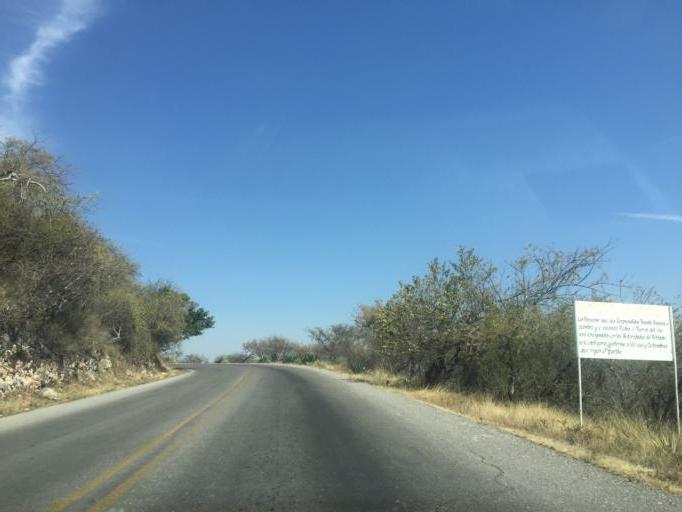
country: MX
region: Morelos
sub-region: Miacatlan
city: Xochicalco (Cirenio Longares)
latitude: 18.7984
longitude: -99.2956
